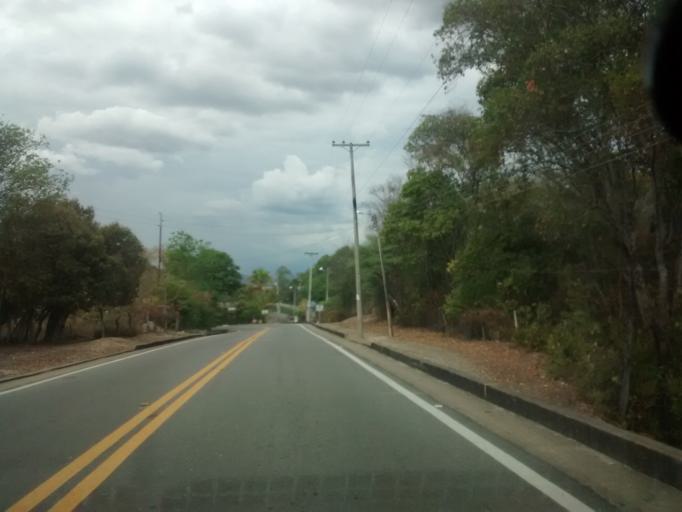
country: CO
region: Cundinamarca
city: Agua de Dios
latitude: 4.4175
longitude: -74.7087
